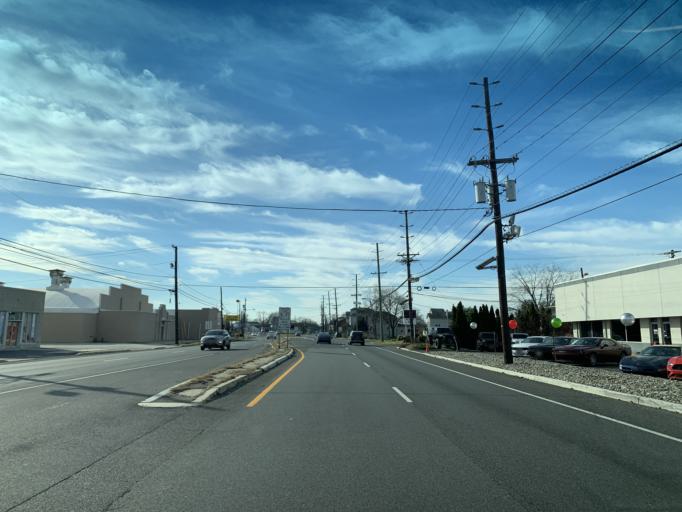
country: US
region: Pennsylvania
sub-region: Bucks County
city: Bristol
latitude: 40.0842
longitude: -74.8358
